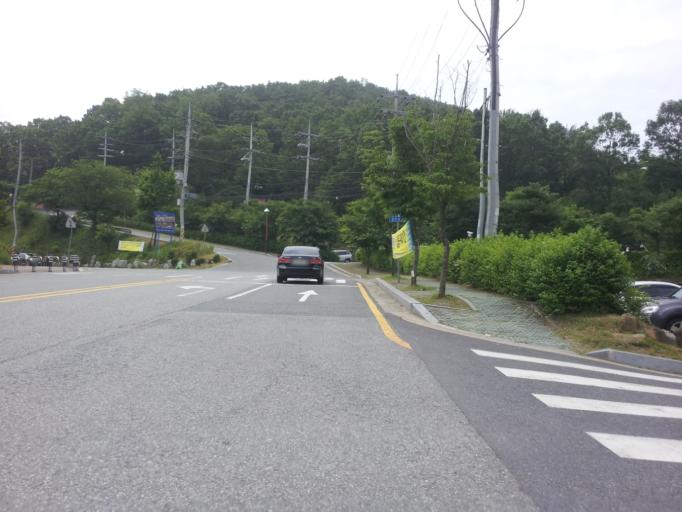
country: KR
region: Daejeon
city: Daejeon
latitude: 36.3314
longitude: 127.4804
